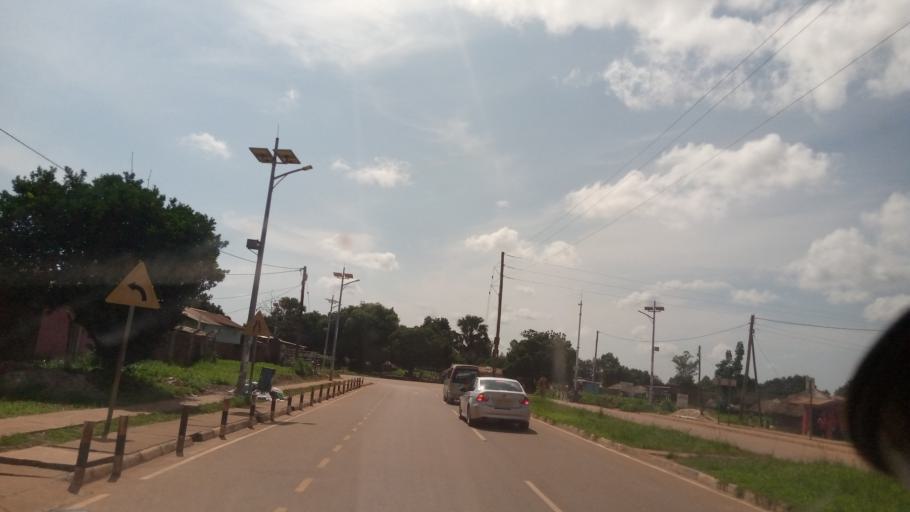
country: UG
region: Northern Region
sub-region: Gulu District
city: Gulu
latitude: 2.7650
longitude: 32.3052
